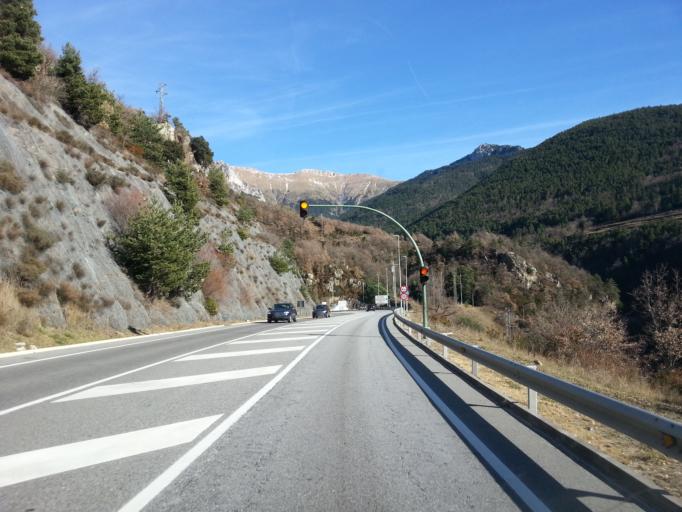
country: ES
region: Catalonia
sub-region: Provincia de Barcelona
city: Baga
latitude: 42.2934
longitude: 1.8604
